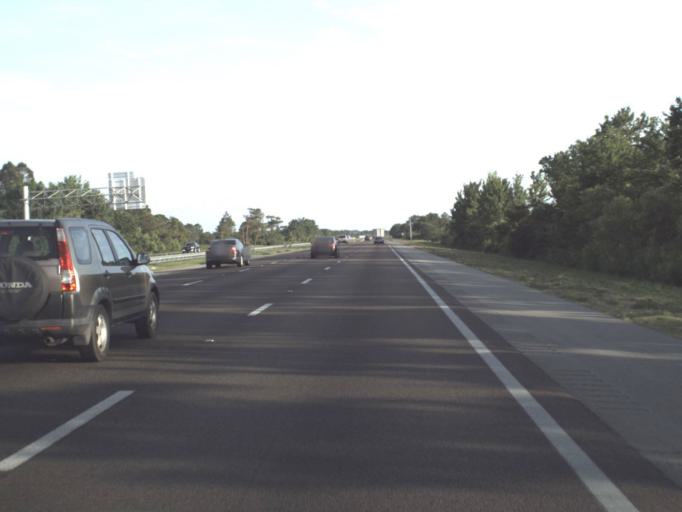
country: US
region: Florida
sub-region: Brevard County
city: Mims
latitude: 28.7544
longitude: -80.8893
